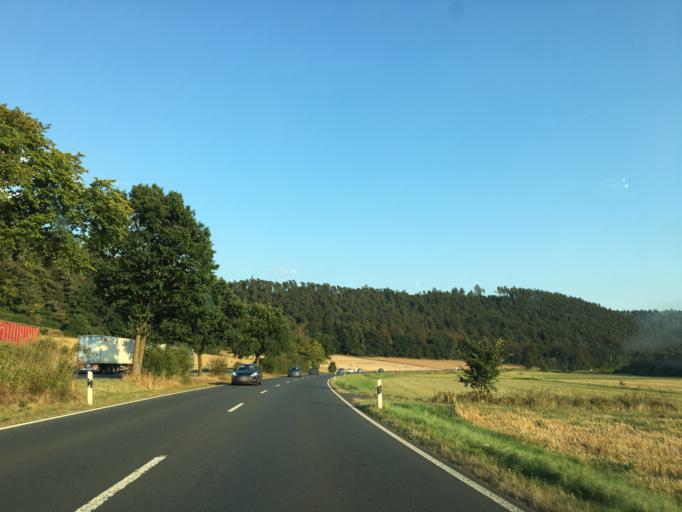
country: DE
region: Hesse
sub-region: Regierungsbezirk Giessen
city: Colbe
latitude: 50.8711
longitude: 8.7865
